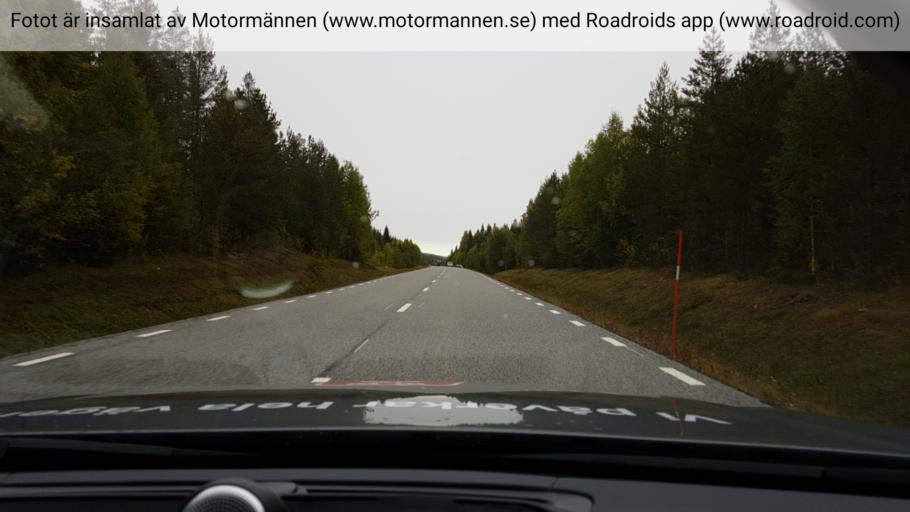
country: SE
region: Jaemtland
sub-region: Stroemsunds Kommun
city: Stroemsund
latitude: 64.0392
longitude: 15.5389
